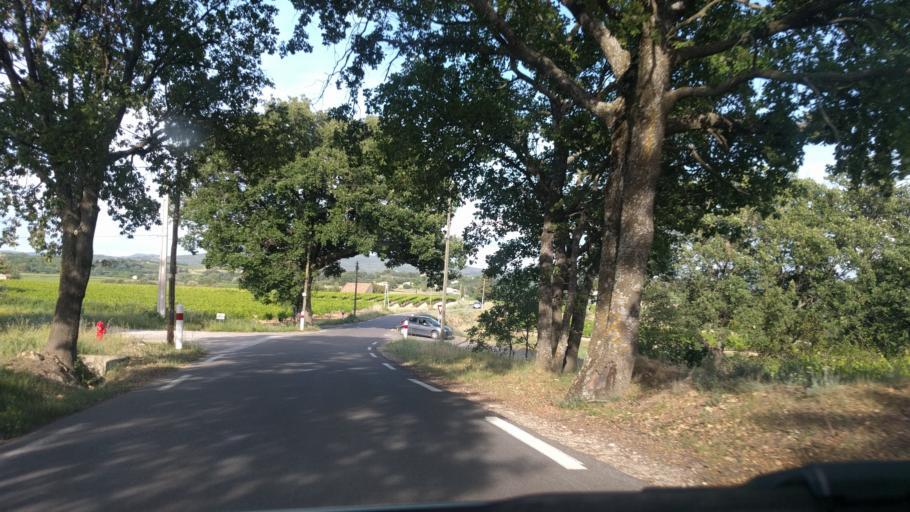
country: FR
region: Provence-Alpes-Cote d'Azur
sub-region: Departement du Vaucluse
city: Pertuis
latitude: 43.7335
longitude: 5.5242
